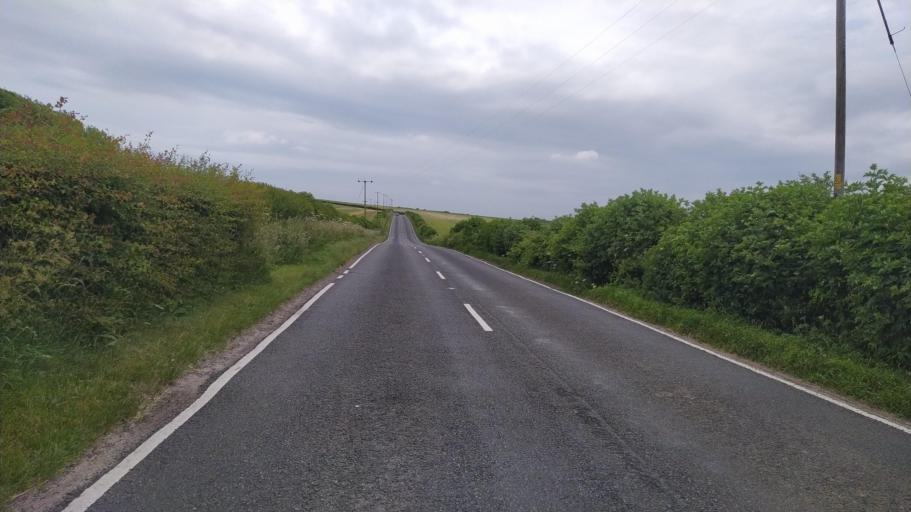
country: GB
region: England
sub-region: Dorset
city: Dorchester
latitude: 50.7669
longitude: -2.4497
